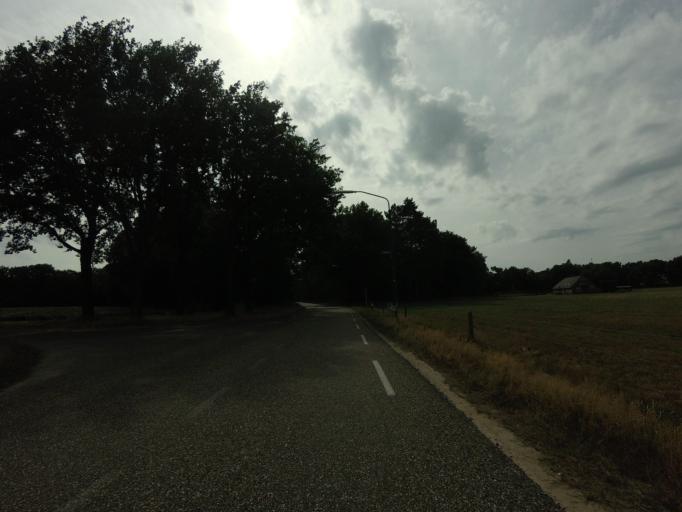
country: NL
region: North Brabant
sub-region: Gemeente Helmond
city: Helmond
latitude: 51.5071
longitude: 5.7563
